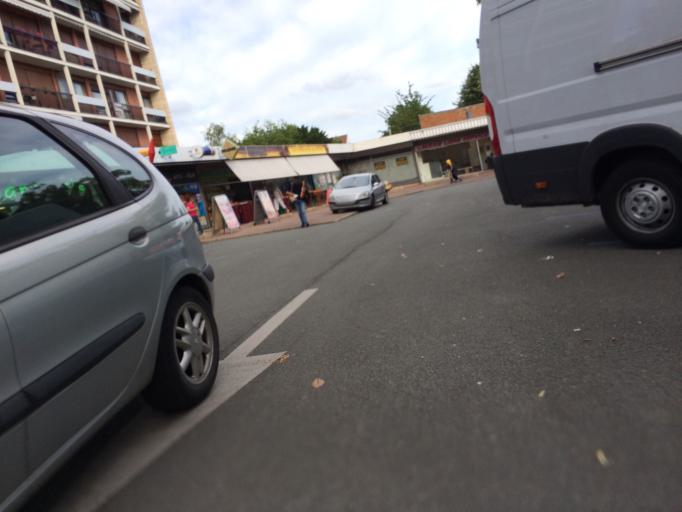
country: FR
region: Ile-de-France
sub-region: Departement de l'Essonne
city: Chilly-Mazarin
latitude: 48.7055
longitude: 2.3151
